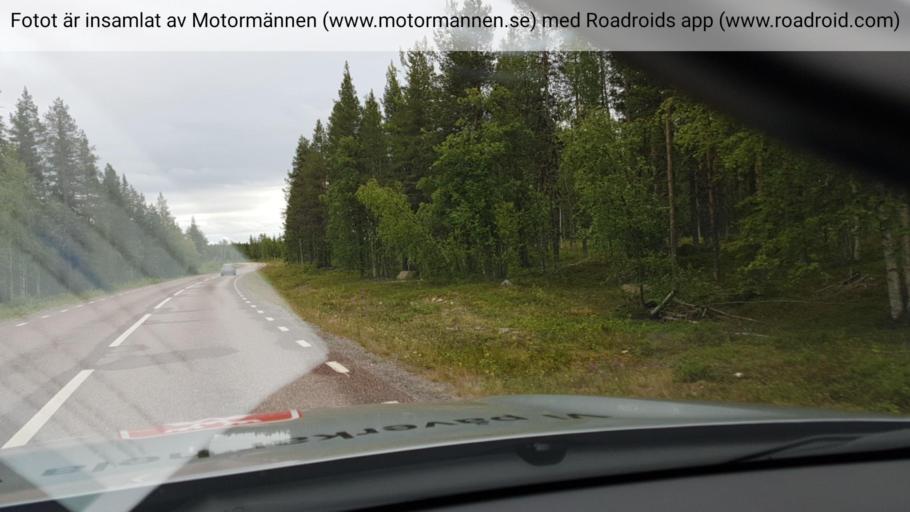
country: SE
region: Norrbotten
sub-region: Gallivare Kommun
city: Gaellivare
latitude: 67.0609
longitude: 21.5767
